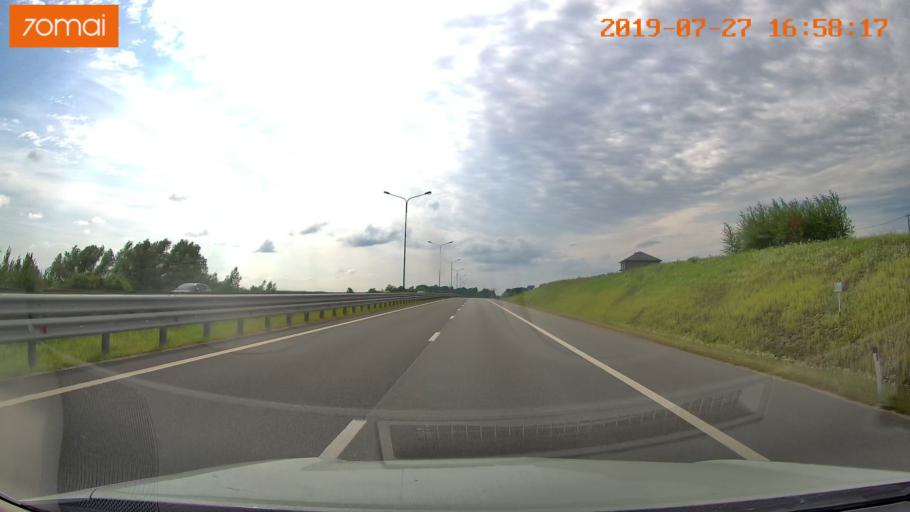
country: RU
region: Kaliningrad
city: Bol'shoe Isakovo
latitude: 54.7012
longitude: 20.6859
